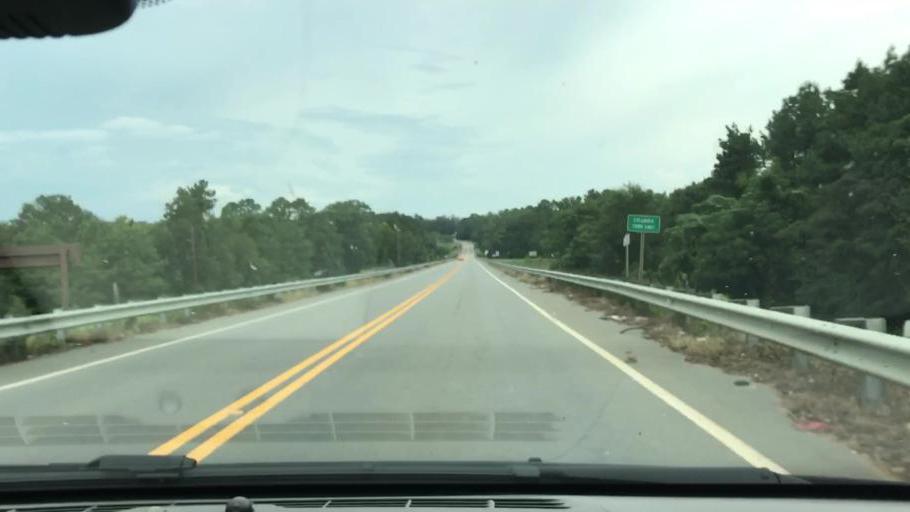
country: US
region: Alabama
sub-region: Houston County
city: Ashford
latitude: 31.2857
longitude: -85.1009
